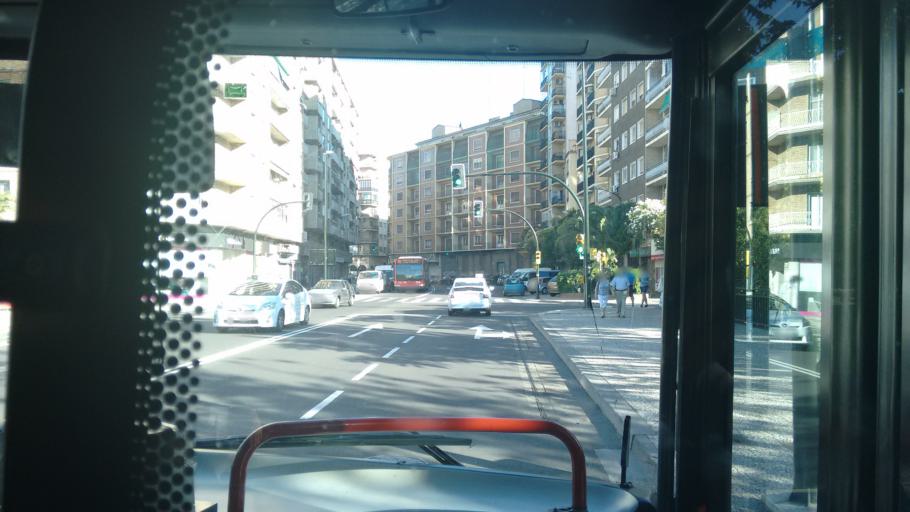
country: ES
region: Aragon
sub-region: Provincia de Zaragoza
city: Zaragoza
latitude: 41.6488
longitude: -0.8759
